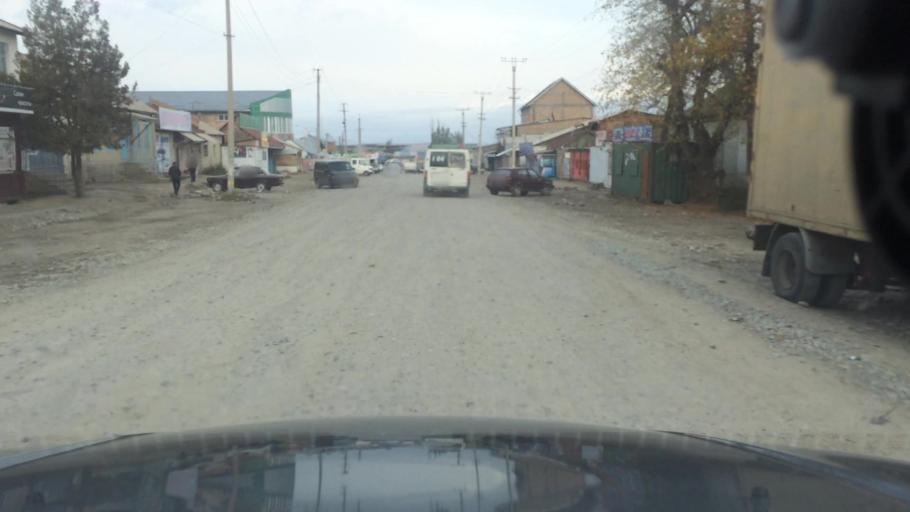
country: KG
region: Ysyk-Koel
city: Karakol
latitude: 42.4911
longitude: 78.3868
